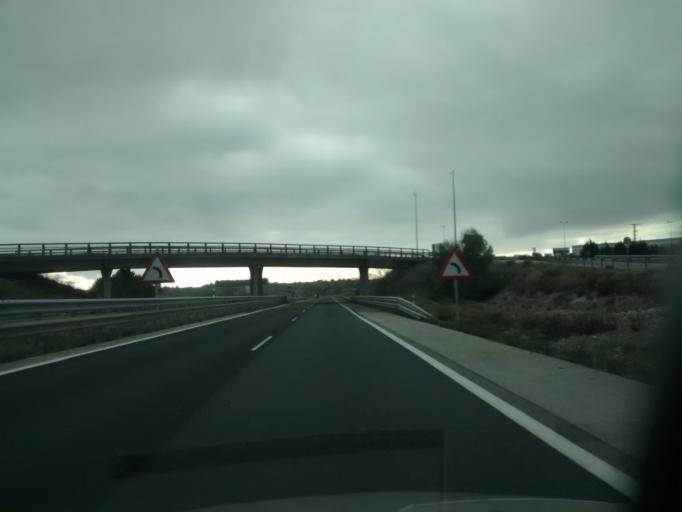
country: ES
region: Castille-La Mancha
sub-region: Provincia de Guadalajara
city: Torija
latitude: 40.7484
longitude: -3.0294
